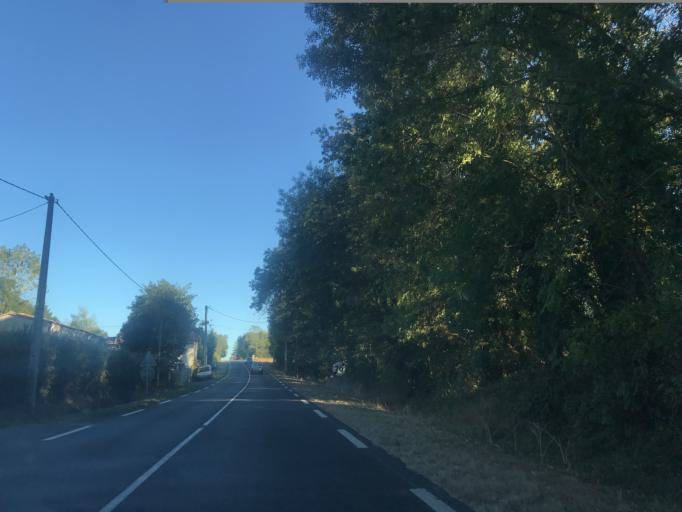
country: FR
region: Poitou-Charentes
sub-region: Departement de la Charente-Maritime
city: Montguyon
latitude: 45.1812
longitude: -0.1244
